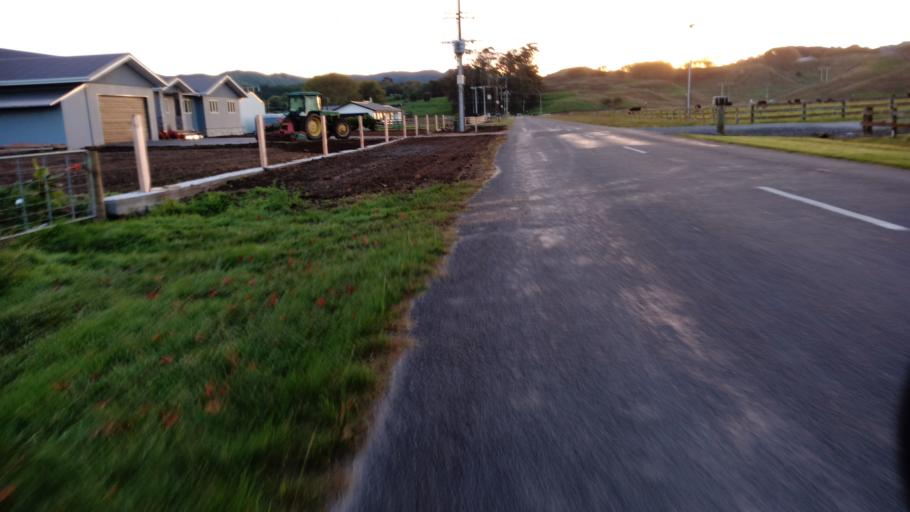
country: NZ
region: Gisborne
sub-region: Gisborne District
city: Gisborne
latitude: -38.6330
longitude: 177.9886
